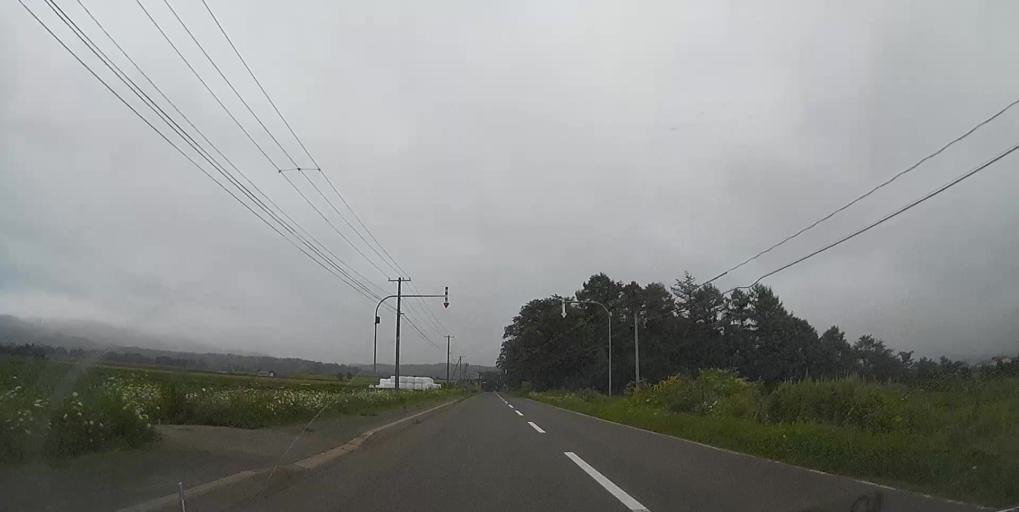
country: JP
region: Hokkaido
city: Iwanai
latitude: 42.4355
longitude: 139.9877
